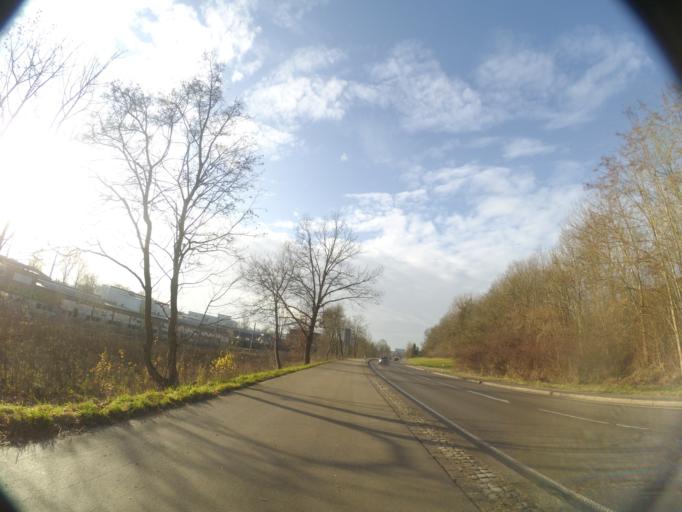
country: DE
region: Baden-Wuerttemberg
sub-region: Tuebingen Region
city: Ulm
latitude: 48.3714
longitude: 9.9488
